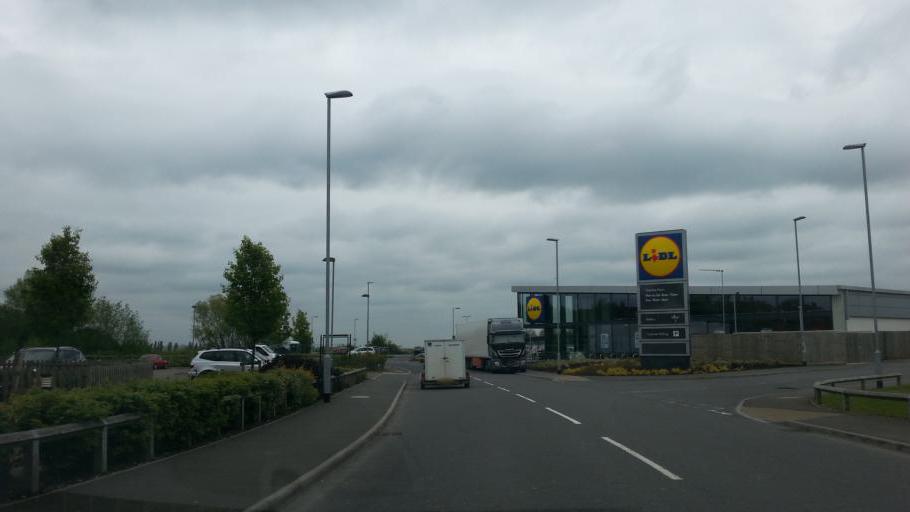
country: GB
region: England
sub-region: Lincolnshire
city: Bourne
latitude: 52.7553
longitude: -0.3691
